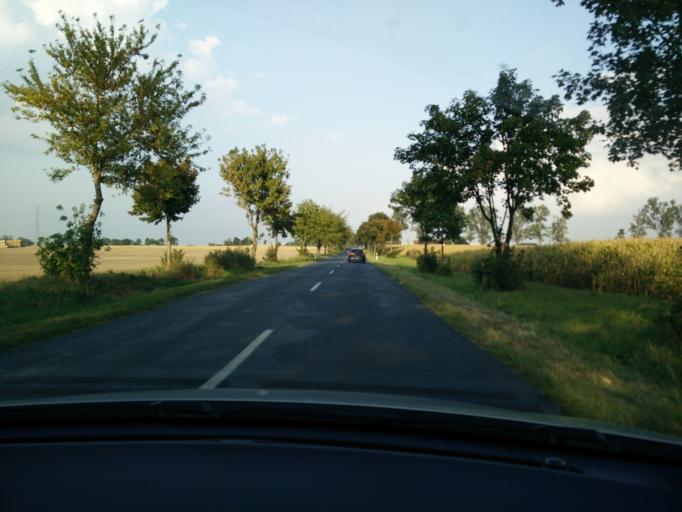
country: PL
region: Greater Poland Voivodeship
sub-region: Powiat wrzesinski
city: Miloslaw
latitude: 52.2840
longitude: 17.4892
